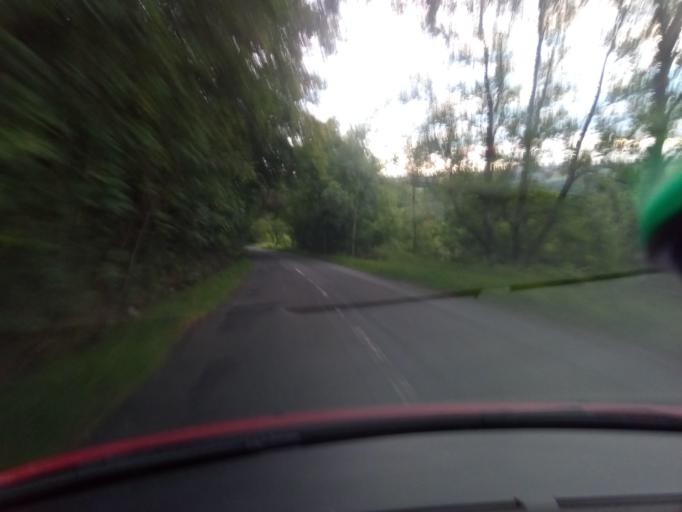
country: GB
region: England
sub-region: Northumberland
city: Bardon Mill
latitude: 54.9057
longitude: -2.3405
